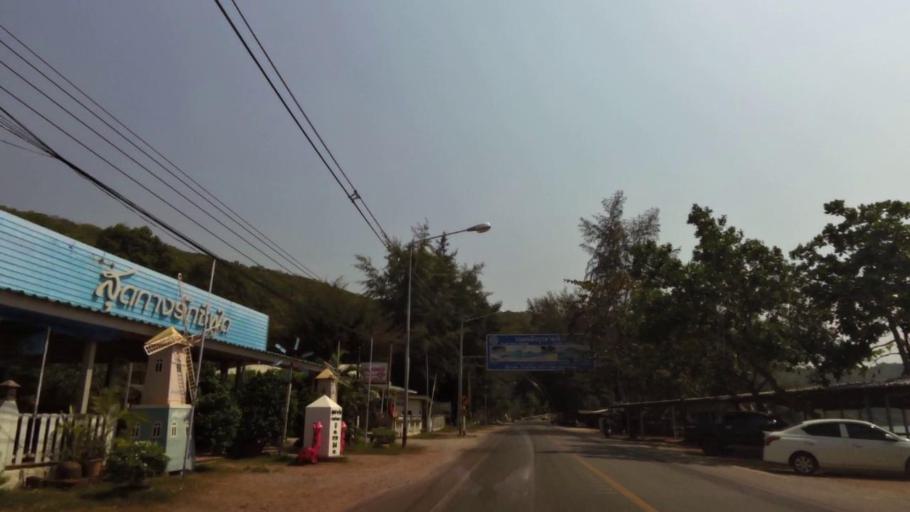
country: TH
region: Chanthaburi
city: Tha Mai
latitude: 12.5328
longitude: 101.9432
